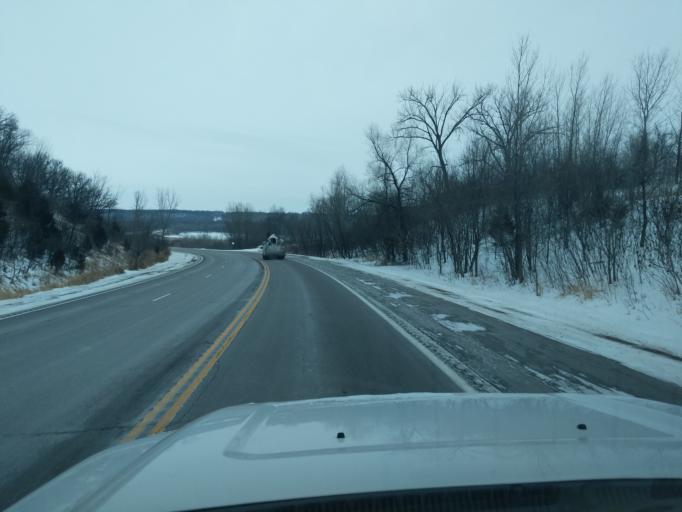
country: US
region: Minnesota
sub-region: Redwood County
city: Redwood Falls
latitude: 44.5600
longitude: -94.9993
